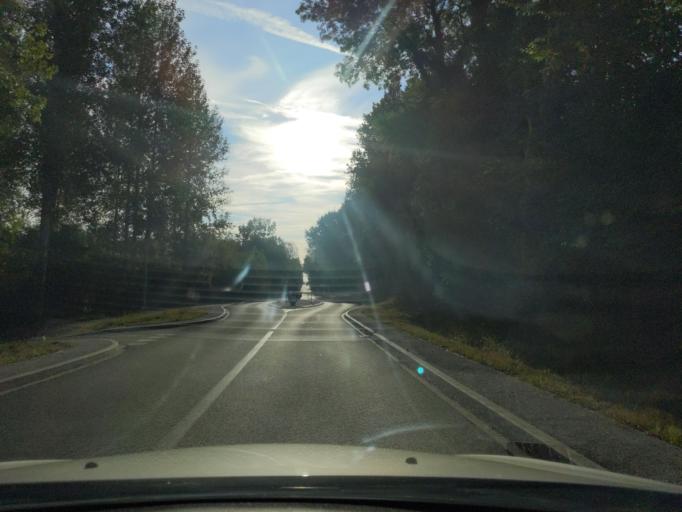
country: FR
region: Poitou-Charentes
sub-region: Departement de la Charente-Maritime
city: Le Gua
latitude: 45.7542
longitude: -0.9574
